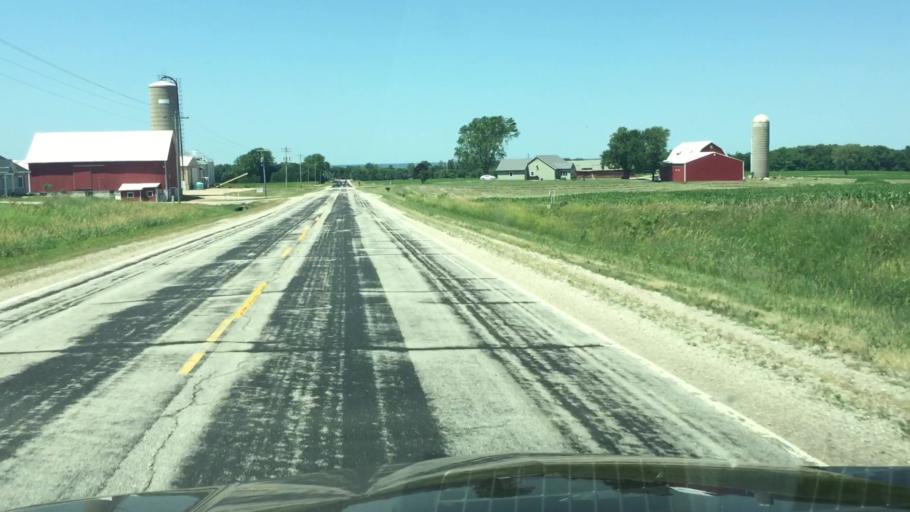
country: US
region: Wisconsin
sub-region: Fond du Lac County
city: Saint Peter
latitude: 43.9697
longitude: -88.2926
